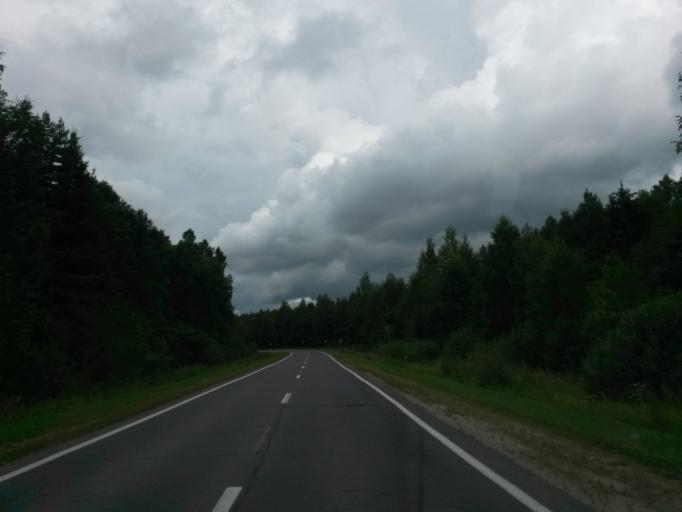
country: RU
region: Jaroslavl
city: Konstantinovskiy
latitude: 57.8557
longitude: 39.6206
